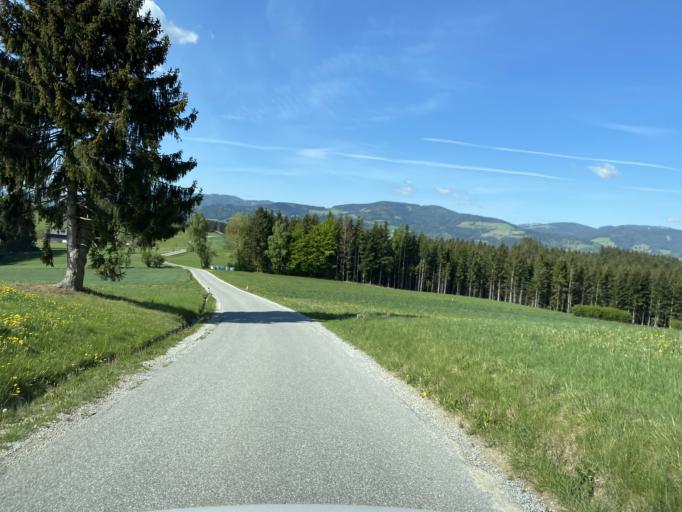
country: AT
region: Styria
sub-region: Politischer Bezirk Weiz
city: Strallegg
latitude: 47.3750
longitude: 15.7202
